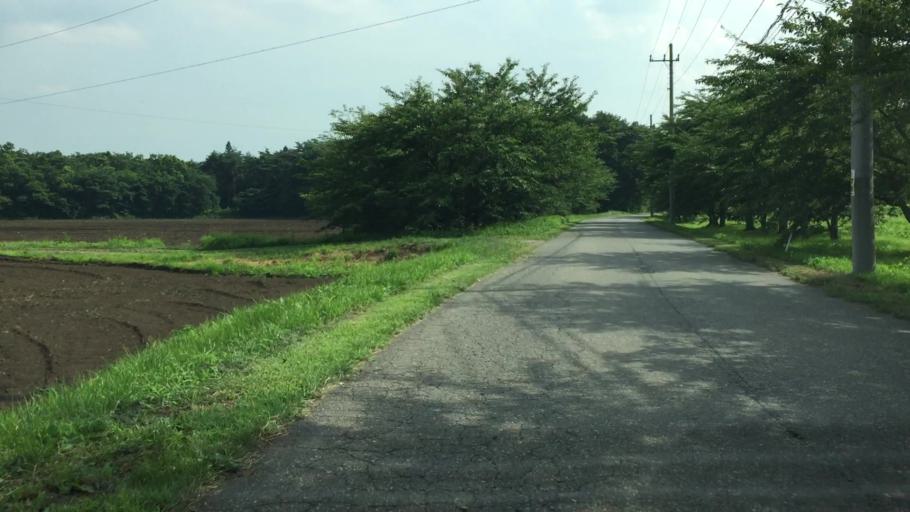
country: JP
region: Tochigi
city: Kuroiso
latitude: 37.0419
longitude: 139.9529
